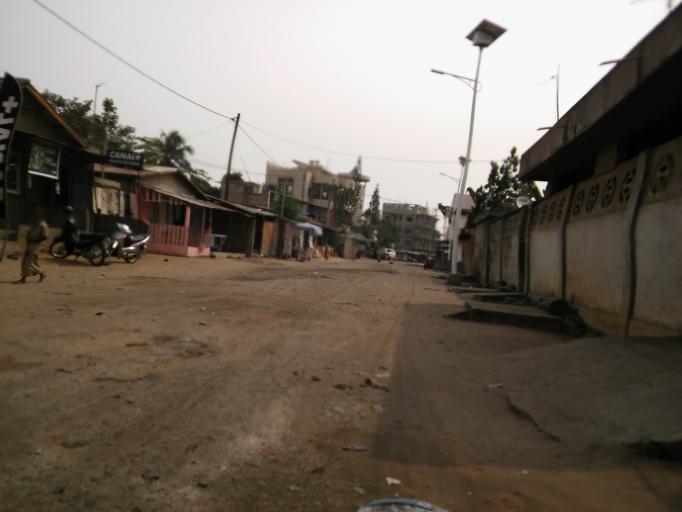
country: BJ
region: Littoral
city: Cotonou
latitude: 6.3930
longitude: 2.3797
